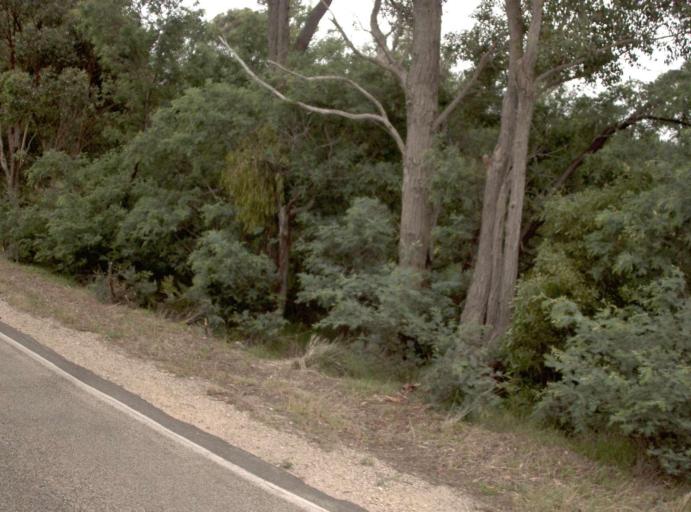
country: AU
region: Victoria
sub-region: East Gippsland
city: Bairnsdale
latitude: -37.8388
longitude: 147.4317
